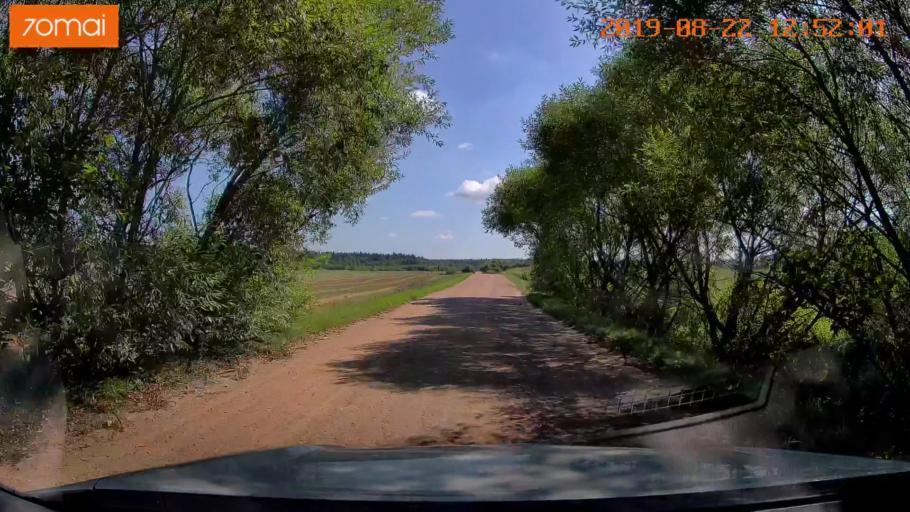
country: BY
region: Minsk
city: Prawdzinski
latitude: 53.4546
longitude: 27.6645
